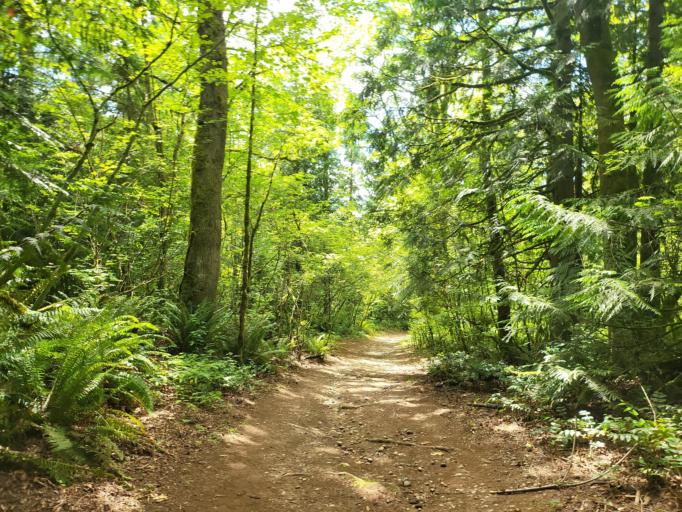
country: US
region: Washington
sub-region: King County
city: Newcastle
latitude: 47.5352
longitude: -122.1261
